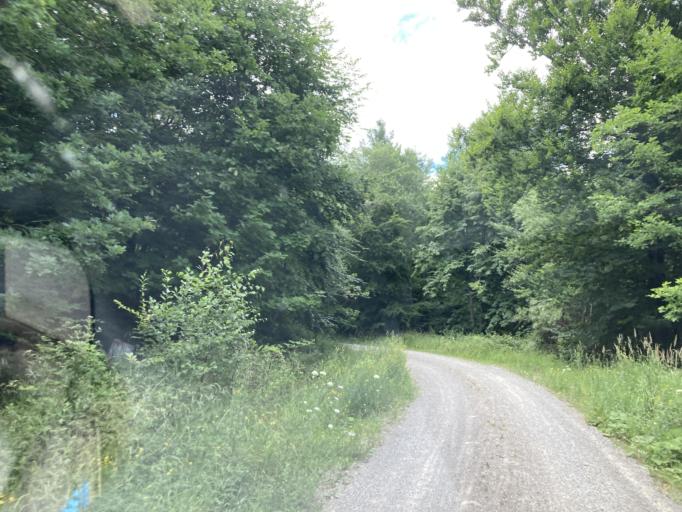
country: DE
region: Baden-Wuerttemberg
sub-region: Tuebingen Region
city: Ofterdingen
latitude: 48.4429
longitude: 9.0143
